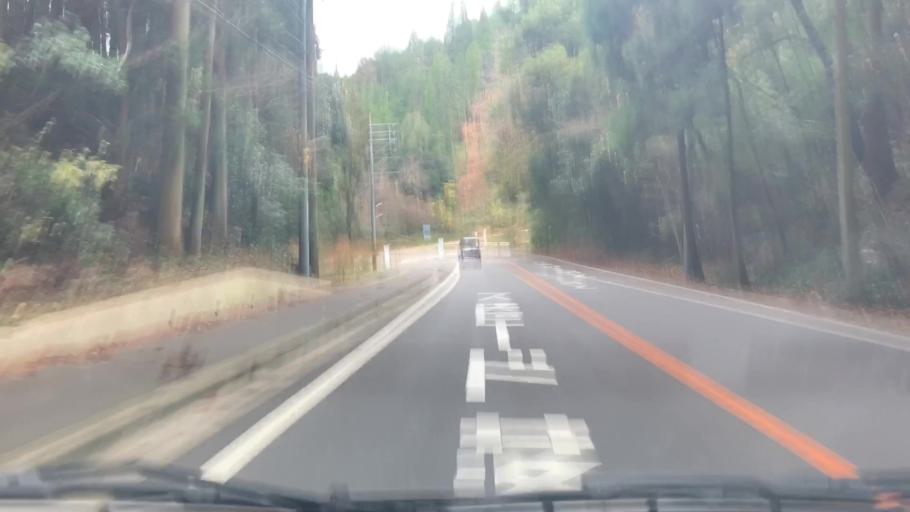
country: JP
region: Saga Prefecture
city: Takeocho-takeo
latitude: 33.1820
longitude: 129.9707
